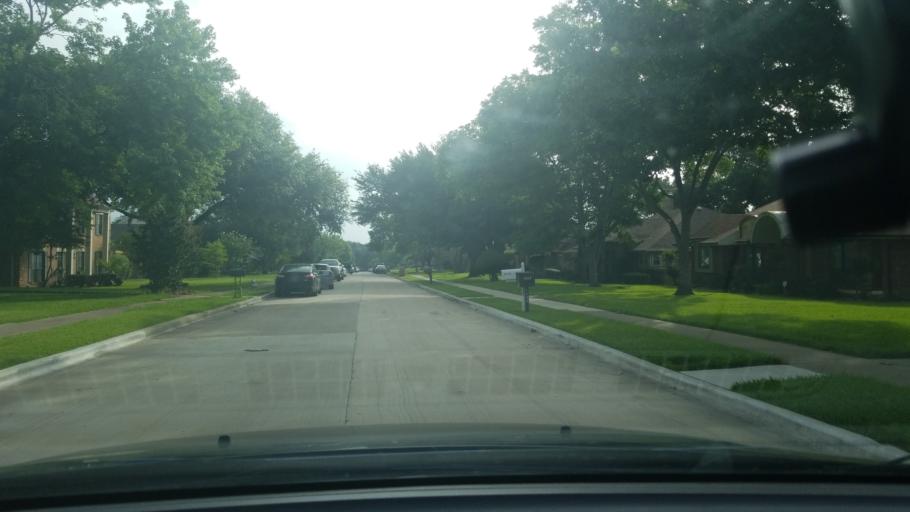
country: US
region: Texas
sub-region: Dallas County
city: Mesquite
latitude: 32.7859
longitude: -96.6476
